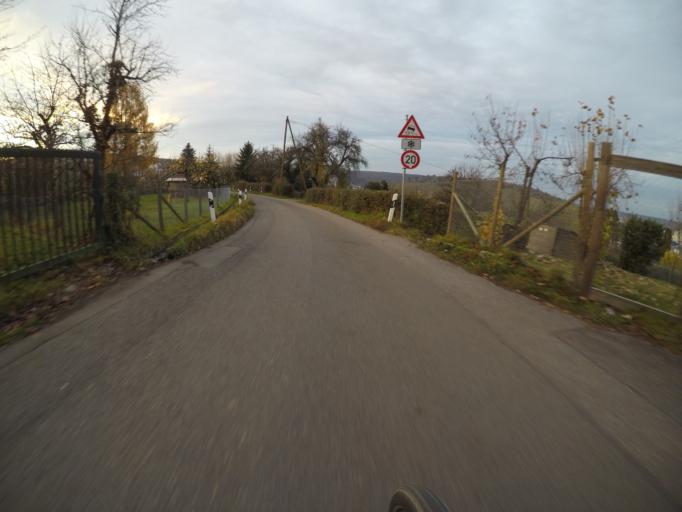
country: DE
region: Baden-Wuerttemberg
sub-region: Regierungsbezirk Stuttgart
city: Ostfildern
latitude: 48.7516
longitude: 9.2524
